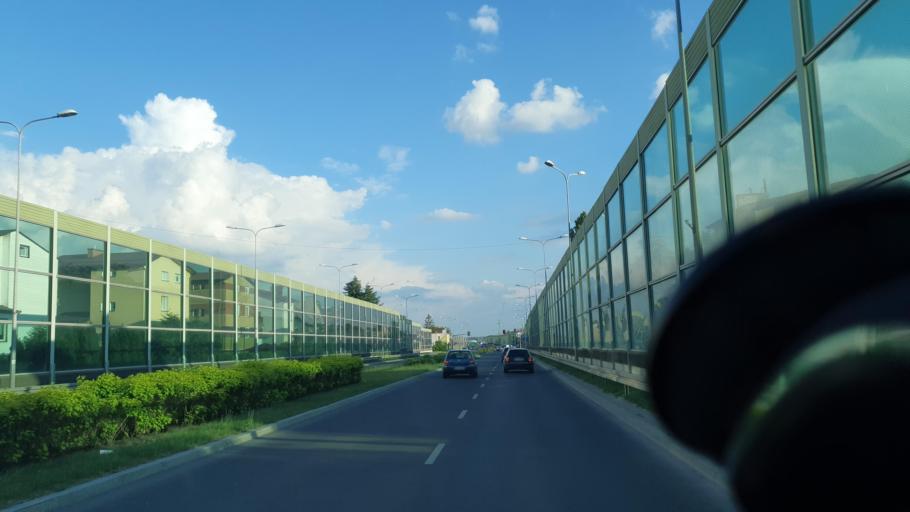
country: PL
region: Podlasie
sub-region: Bialystok
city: Bialystok
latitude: 53.1507
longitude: 23.2019
